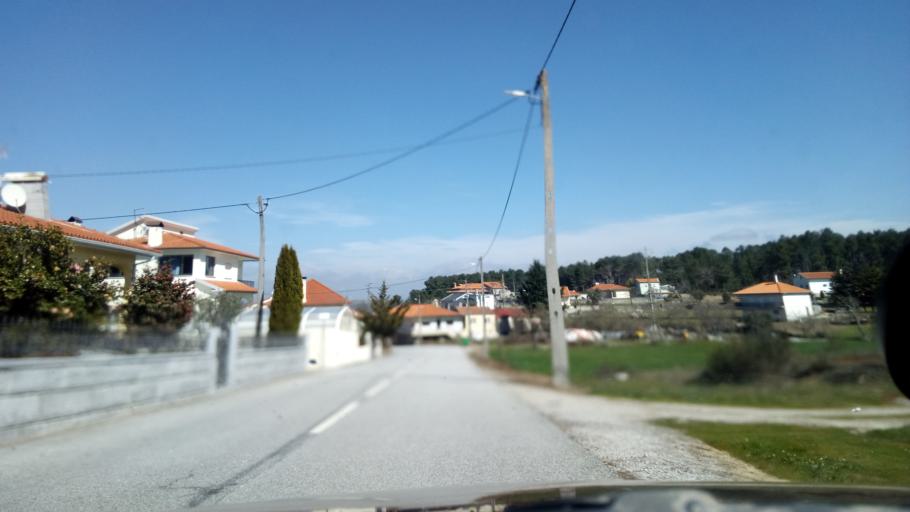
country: PT
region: Guarda
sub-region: Fornos de Algodres
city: Fornos de Algodres
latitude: 40.6460
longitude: -7.5318
